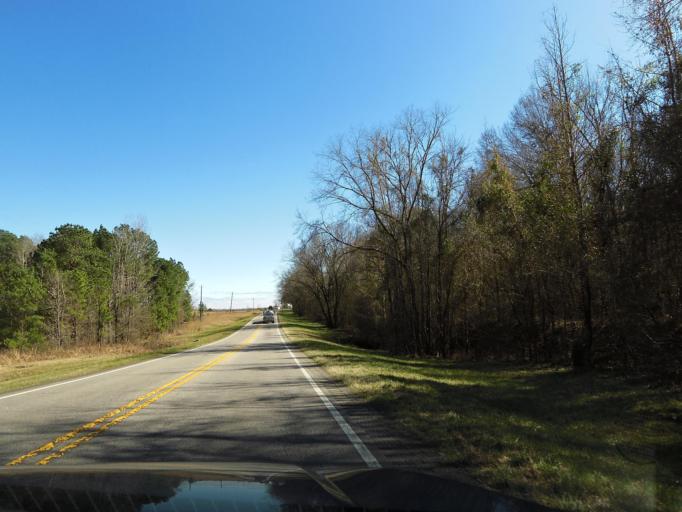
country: US
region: Alabama
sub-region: Bullock County
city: Union Springs
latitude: 32.0930
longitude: -85.5548
